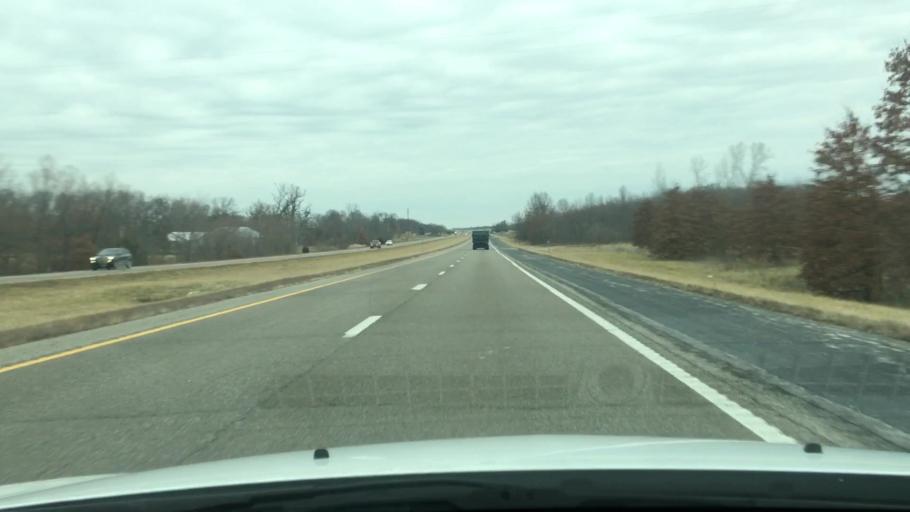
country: US
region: Missouri
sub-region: Audrain County
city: Mexico
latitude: 39.0453
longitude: -91.8935
